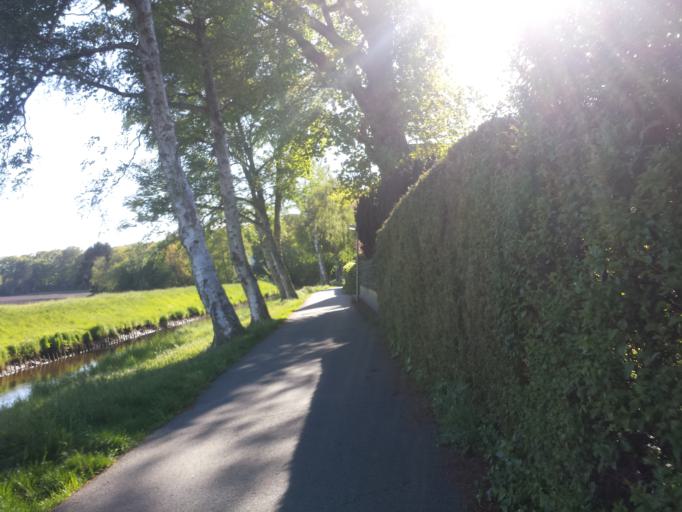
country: DE
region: Lower Saxony
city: Lilienthal
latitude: 53.1470
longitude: 8.9186
